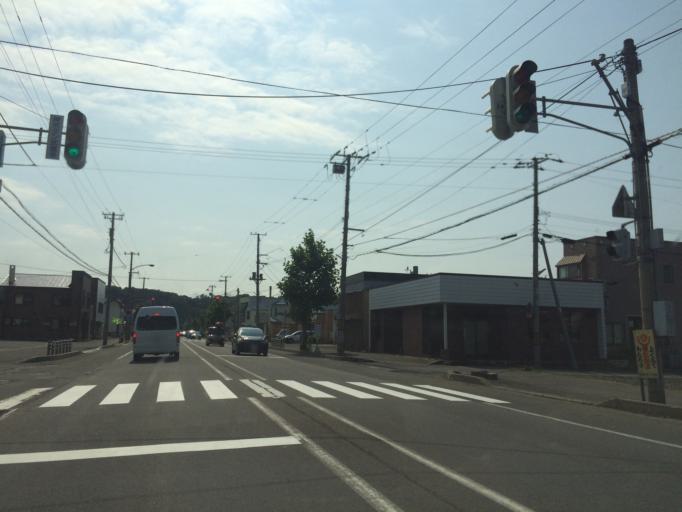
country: JP
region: Hokkaido
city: Yoichi
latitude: 43.1980
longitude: 140.8559
